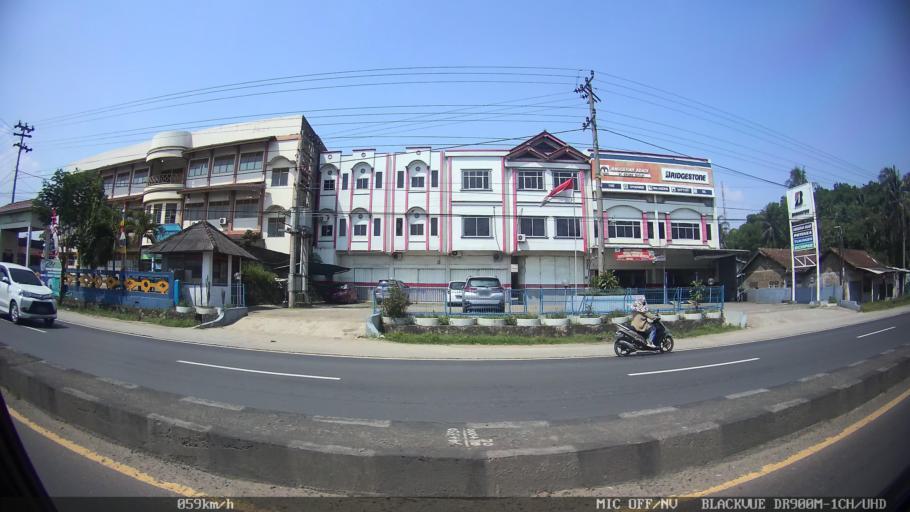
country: ID
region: Lampung
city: Natar
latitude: -5.3473
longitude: 105.2169
